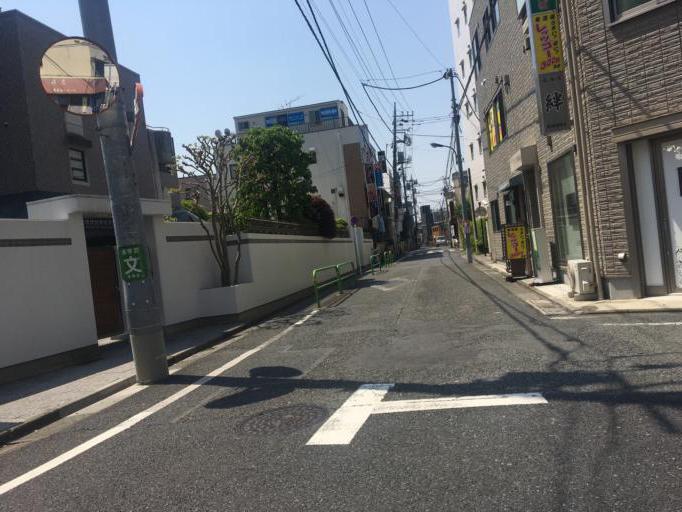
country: JP
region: Saitama
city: Wako
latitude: 35.7774
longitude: 139.6288
